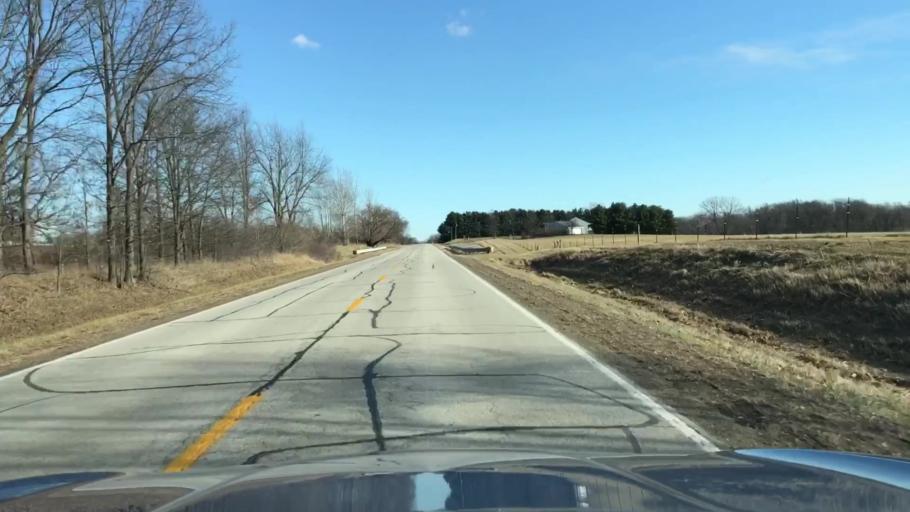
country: US
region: Illinois
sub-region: McLean County
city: Lexington
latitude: 40.6482
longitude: -88.8570
